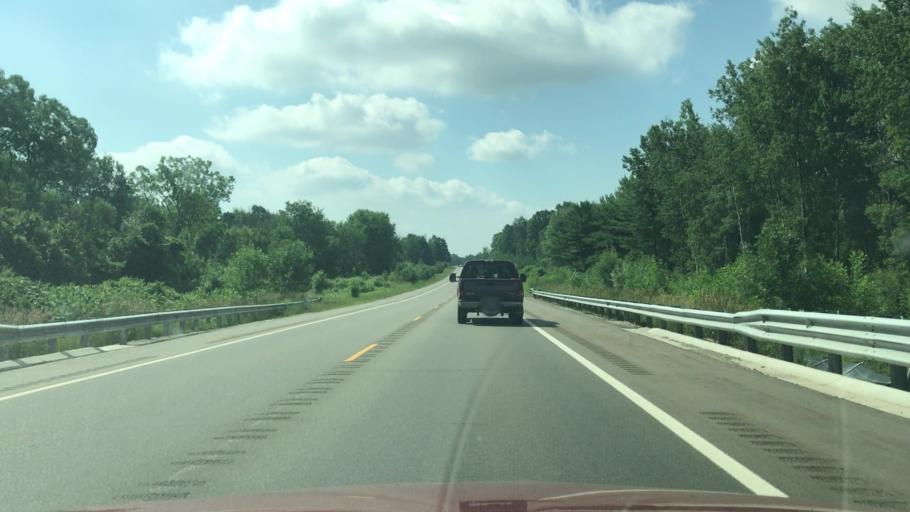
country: US
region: Michigan
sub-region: Kent County
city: Sparta
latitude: 43.1387
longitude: -85.7181
